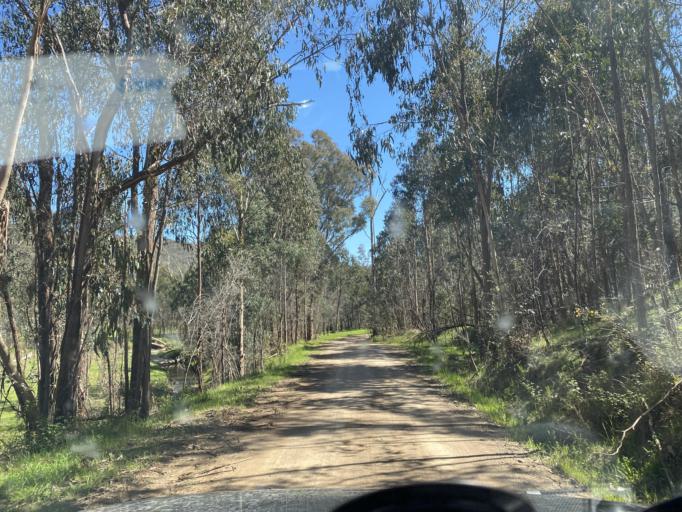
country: AU
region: Victoria
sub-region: Benalla
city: Benalla
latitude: -36.6962
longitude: 146.1777
